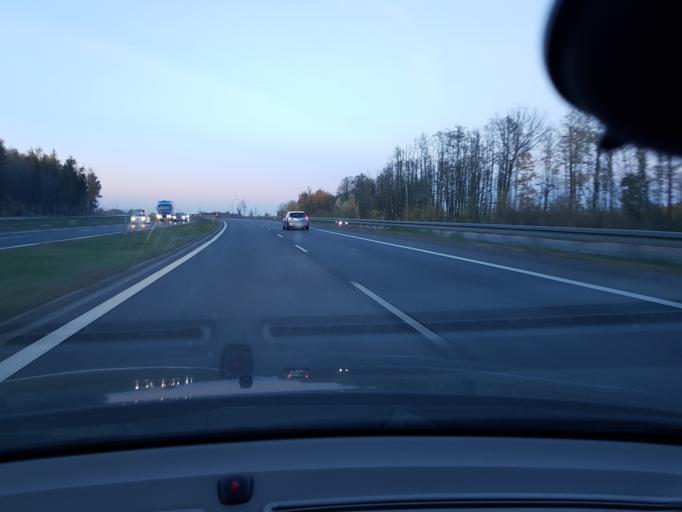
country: PL
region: Masovian Voivodeship
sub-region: Powiat zyrardowski
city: Mszczonow
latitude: 51.9580
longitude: 20.4972
